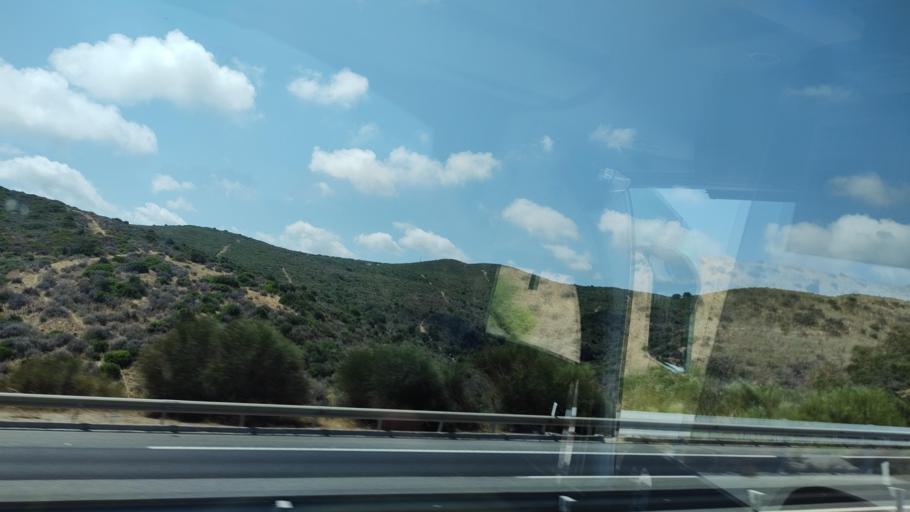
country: ES
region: Andalusia
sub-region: Provincia de Malaga
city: Manilva
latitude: 36.3586
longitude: -5.2684
